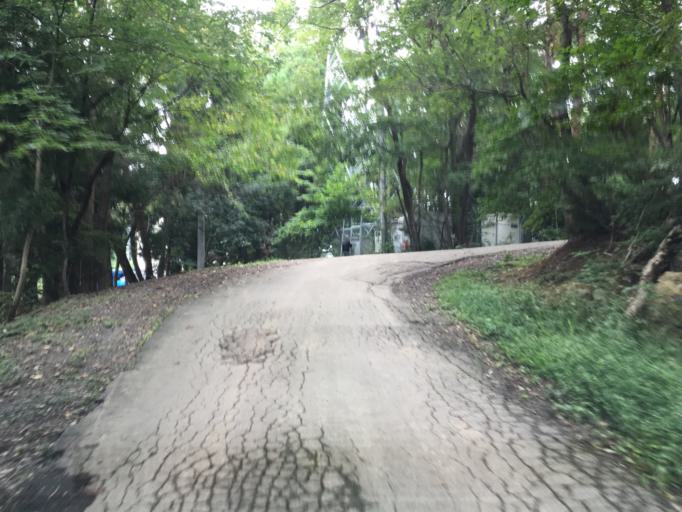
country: JP
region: Fukushima
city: Fukushima-shi
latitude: 37.7751
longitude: 140.4733
